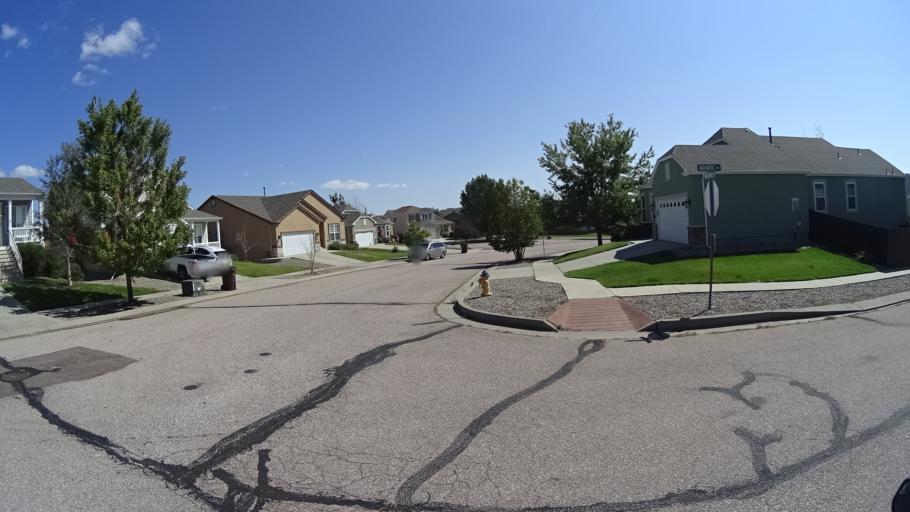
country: US
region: Colorado
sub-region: El Paso County
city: Cimarron Hills
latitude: 38.9254
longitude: -104.7011
